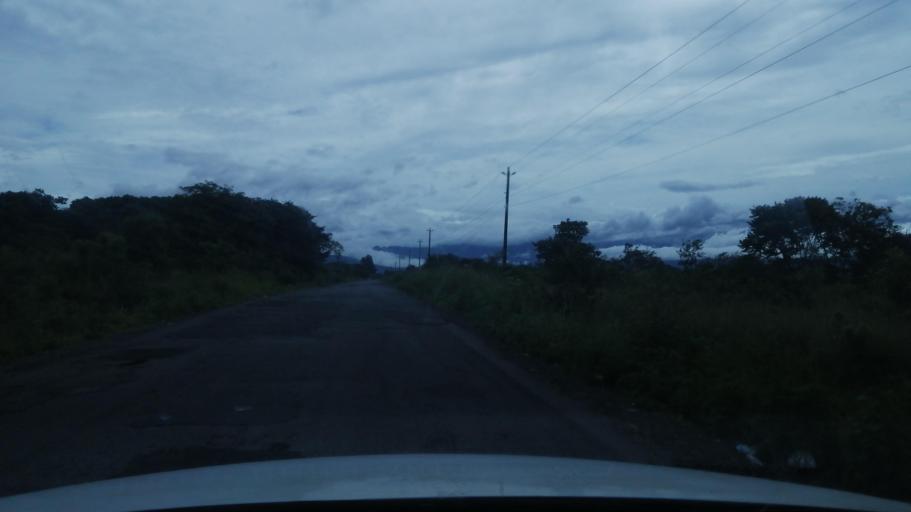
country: PA
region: Chiriqui
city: Potrerillos Abajo
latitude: 8.6689
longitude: -82.4443
